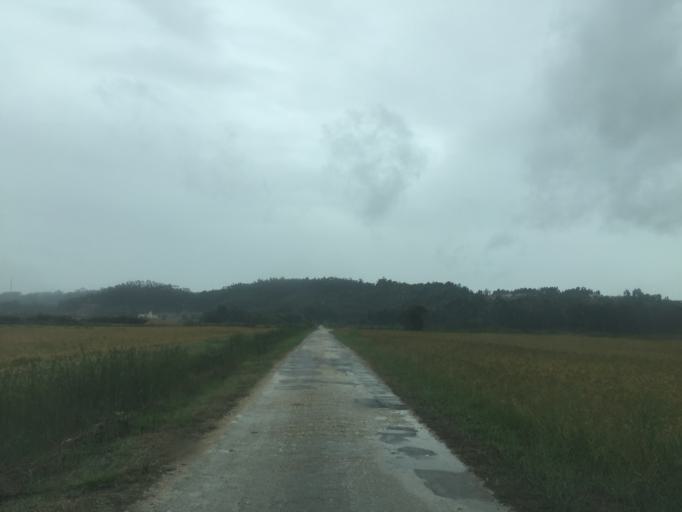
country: PT
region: Coimbra
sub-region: Figueira da Foz
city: Lavos
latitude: 40.0985
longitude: -8.8087
